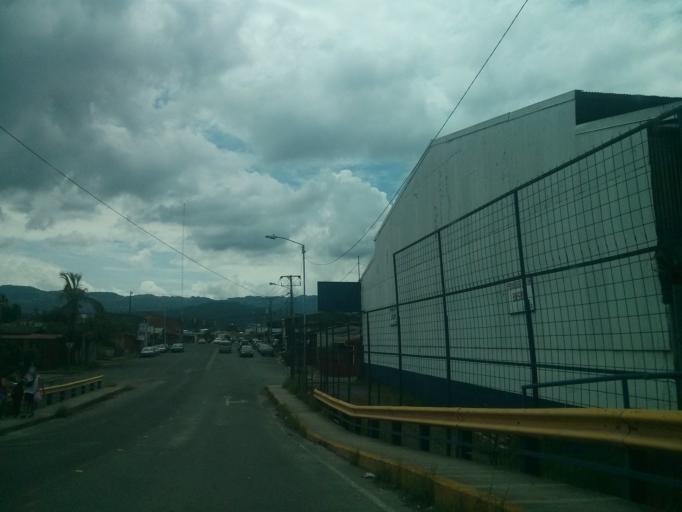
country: CR
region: San Jose
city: San Miguel
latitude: 9.8958
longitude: -84.0562
